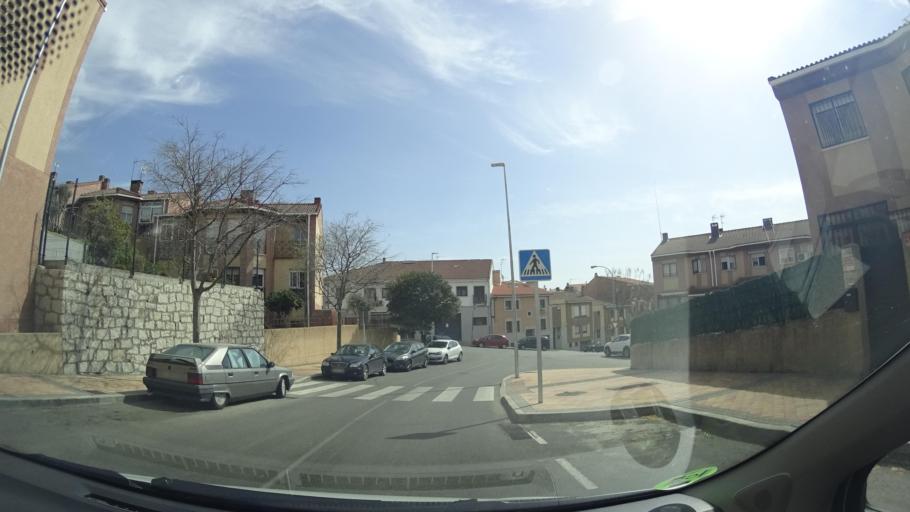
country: ES
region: Madrid
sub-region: Provincia de Madrid
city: Colmenar Viejo
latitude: 40.6557
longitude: -3.7663
